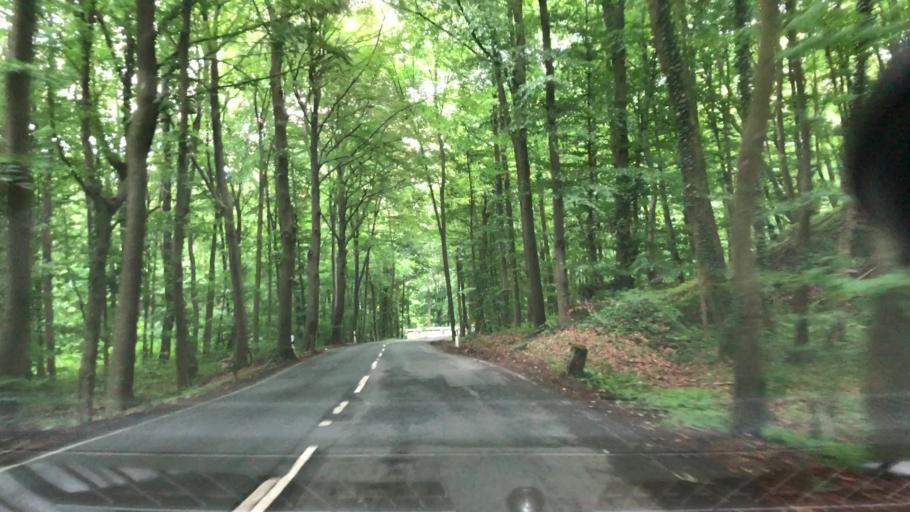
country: DE
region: North Rhine-Westphalia
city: Porta Westfalica
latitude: 52.2487
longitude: 8.9006
